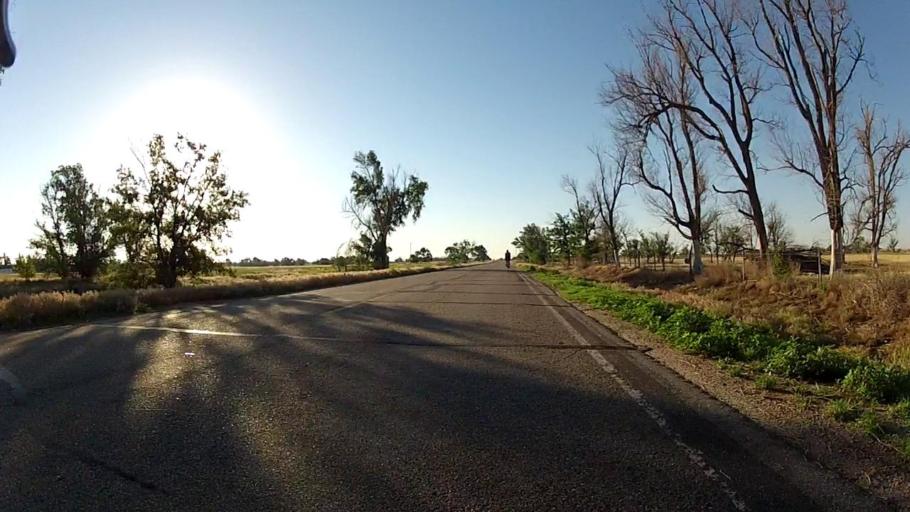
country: US
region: Kansas
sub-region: Ford County
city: Dodge City
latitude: 37.7110
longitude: -99.9196
